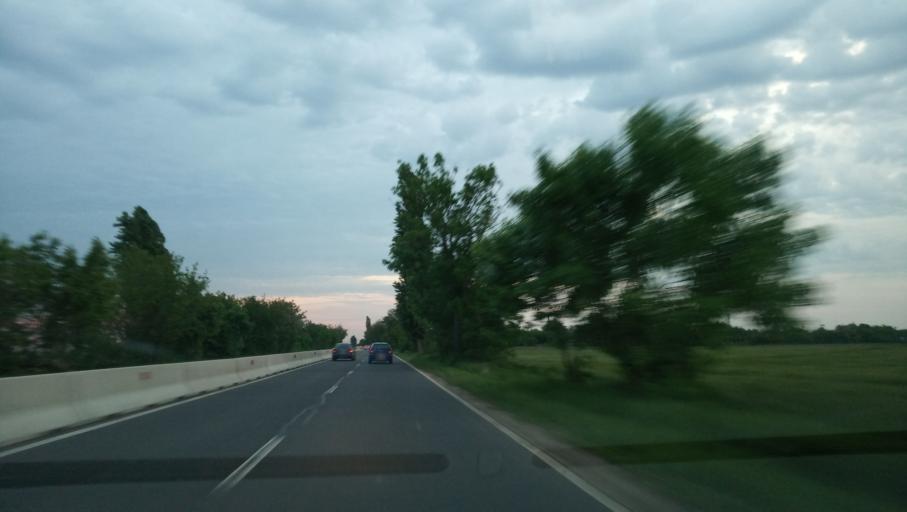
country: RO
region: Timis
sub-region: Comuna Sag
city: Sag
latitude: 45.6653
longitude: 21.1725
